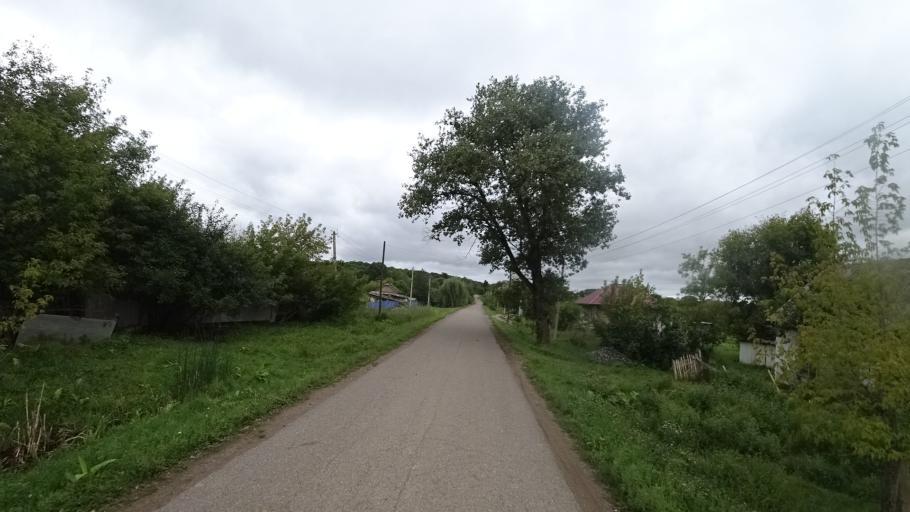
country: RU
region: Primorskiy
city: Chernigovka
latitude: 44.4563
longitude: 132.5907
